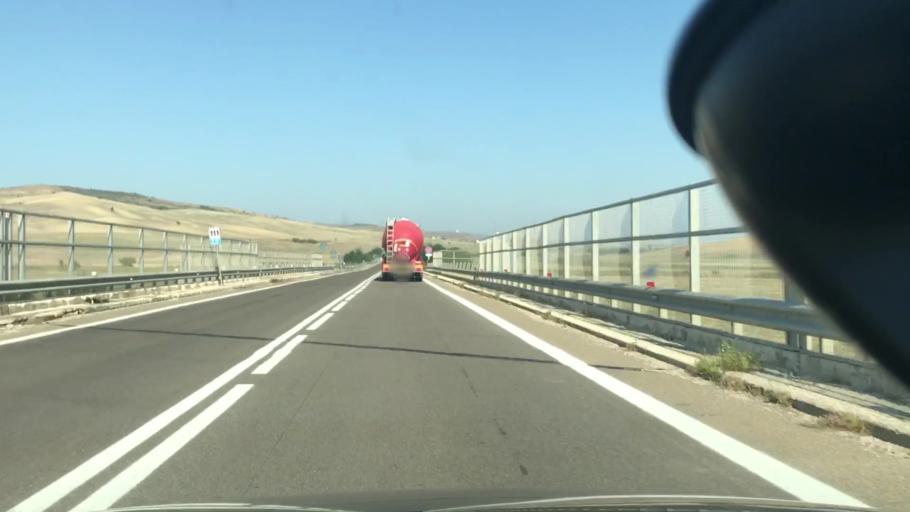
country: IT
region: Basilicate
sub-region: Provincia di Matera
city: Irsina
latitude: 40.7897
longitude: 16.2858
